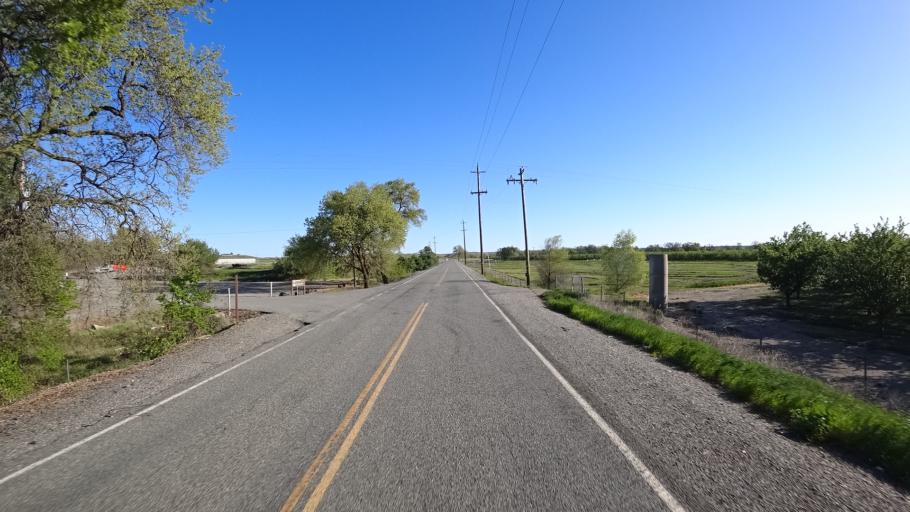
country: US
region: California
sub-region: Glenn County
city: Orland
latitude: 39.8098
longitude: -122.3301
